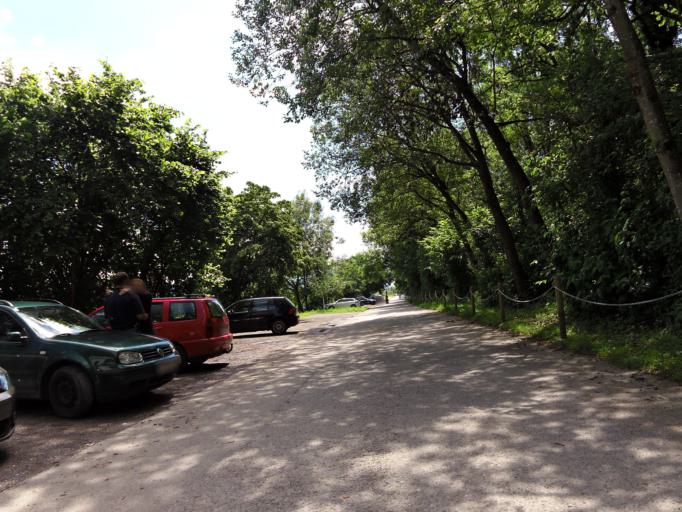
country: AT
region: Vorarlberg
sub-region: Politischer Bezirk Bregenz
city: Hard
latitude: 47.5040
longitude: 9.7015
